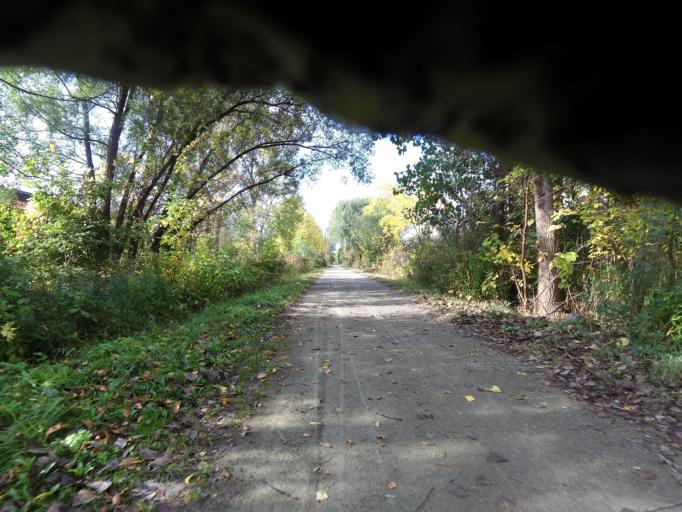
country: CA
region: Ontario
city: Brantford
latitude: 43.1478
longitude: -80.1966
